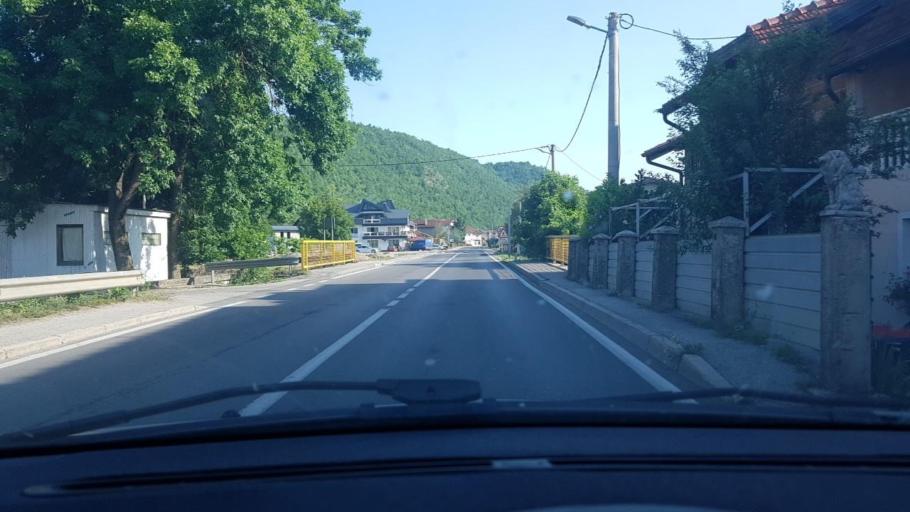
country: BA
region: Federation of Bosnia and Herzegovina
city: Bihac
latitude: 44.8533
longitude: 15.8824
